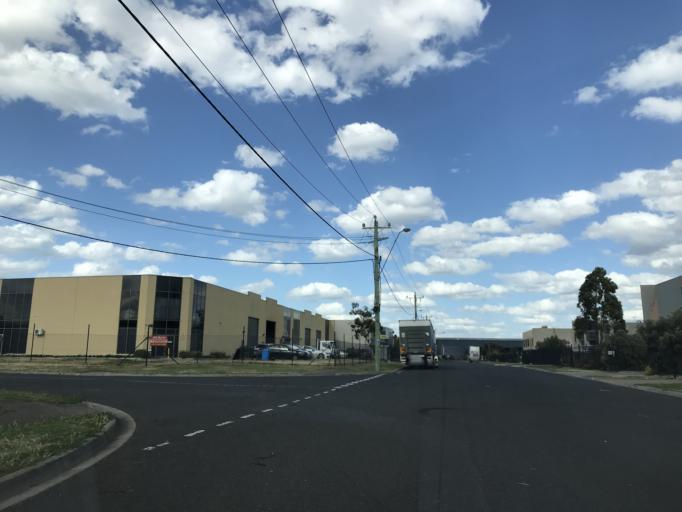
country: AU
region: Victoria
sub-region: Brimbank
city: Sunshine West
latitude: -37.8065
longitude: 144.8127
